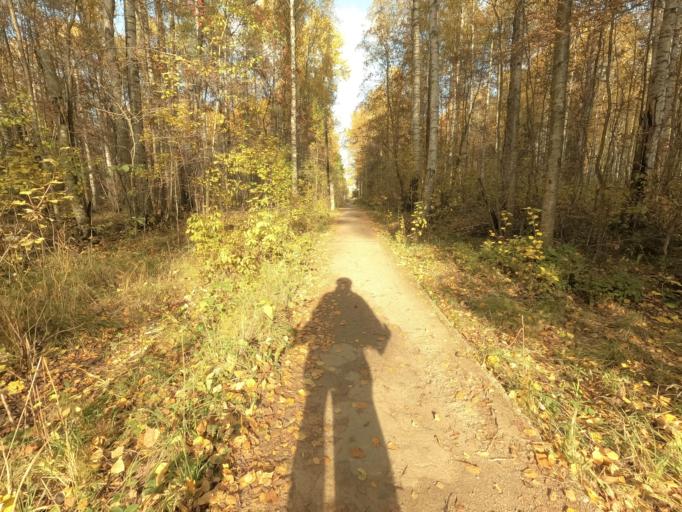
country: RU
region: Leningrad
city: Mga
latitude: 59.7611
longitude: 31.1153
